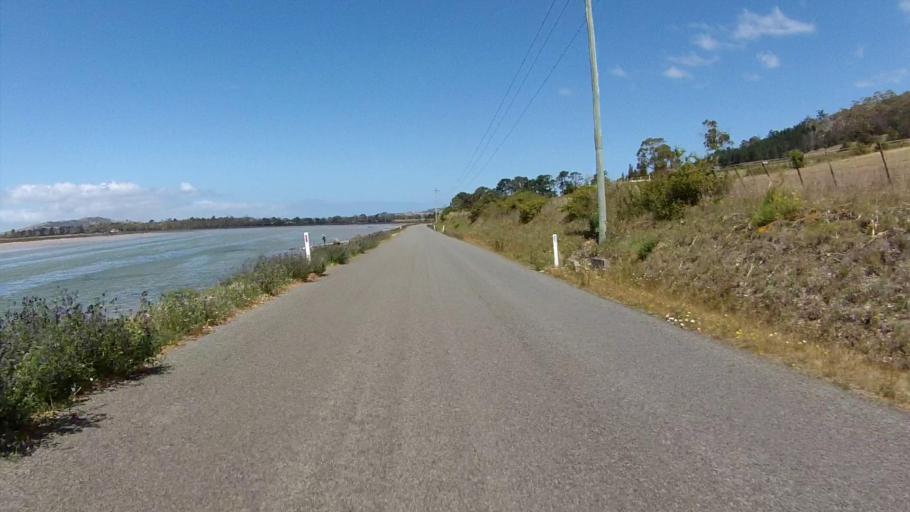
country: AU
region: Tasmania
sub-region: Clarence
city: Lauderdale
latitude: -42.9208
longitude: 147.4798
